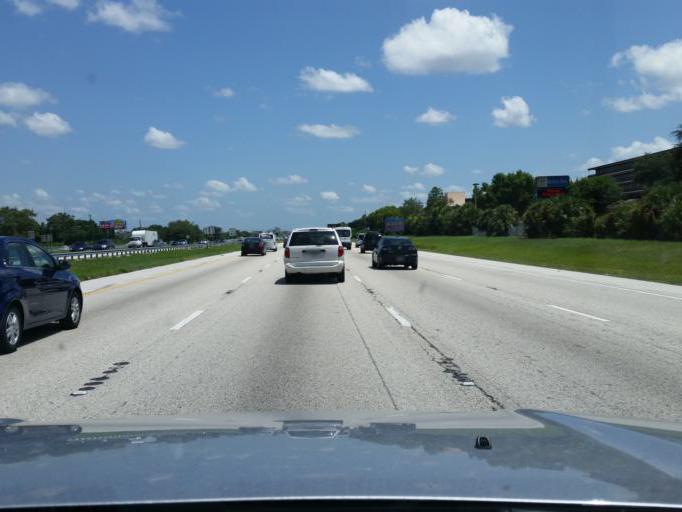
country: US
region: Florida
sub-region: Orange County
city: Doctor Phillips
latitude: 28.4311
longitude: -81.4741
